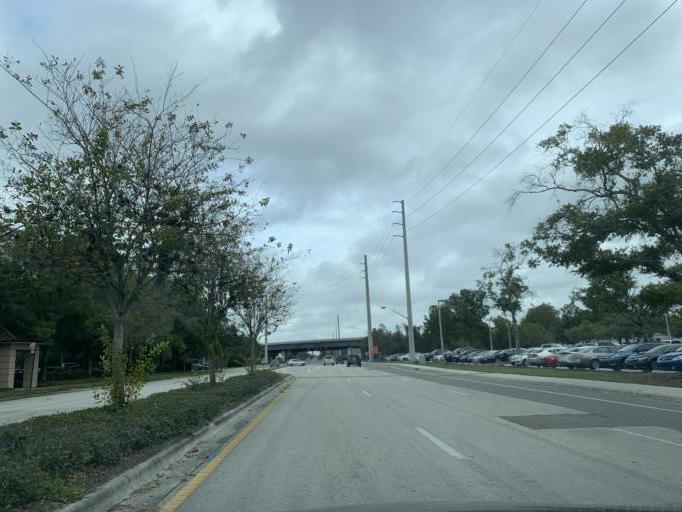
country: US
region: Florida
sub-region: Orange County
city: Eatonville
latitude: 28.6294
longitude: -81.3984
